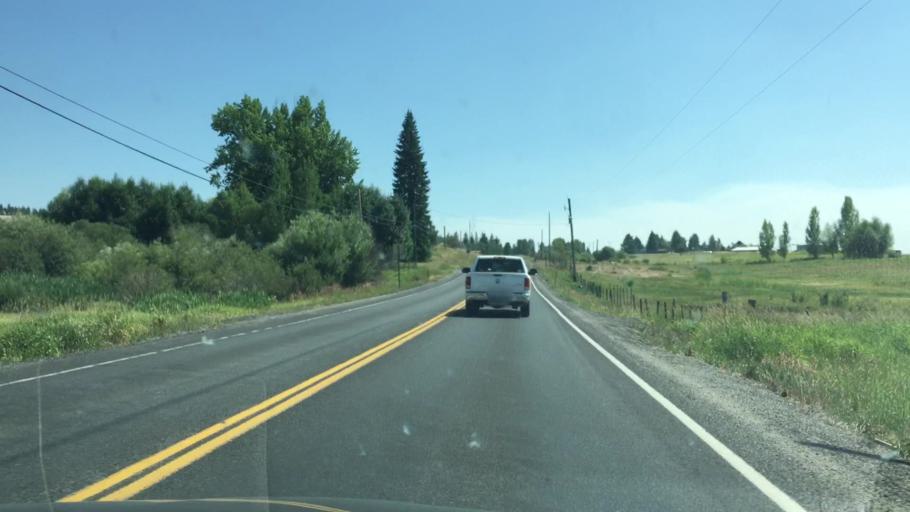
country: US
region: Idaho
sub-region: Valley County
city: McCall
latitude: 44.8892
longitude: -116.0928
